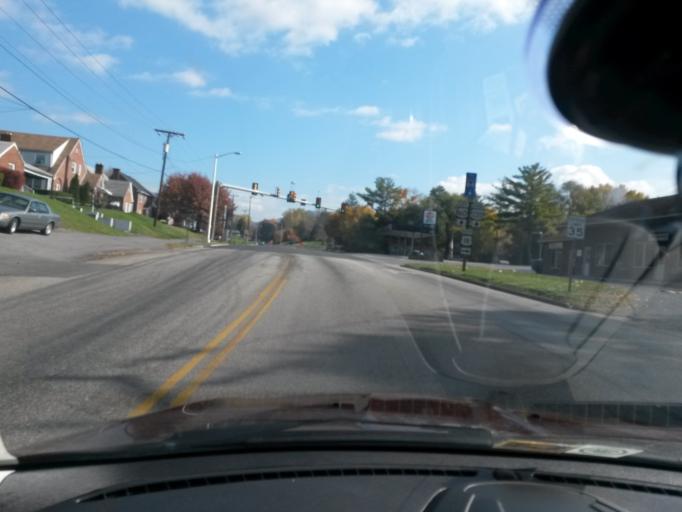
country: US
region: Virginia
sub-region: City of Covington
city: Fairlawn
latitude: 37.7780
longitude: -79.9860
